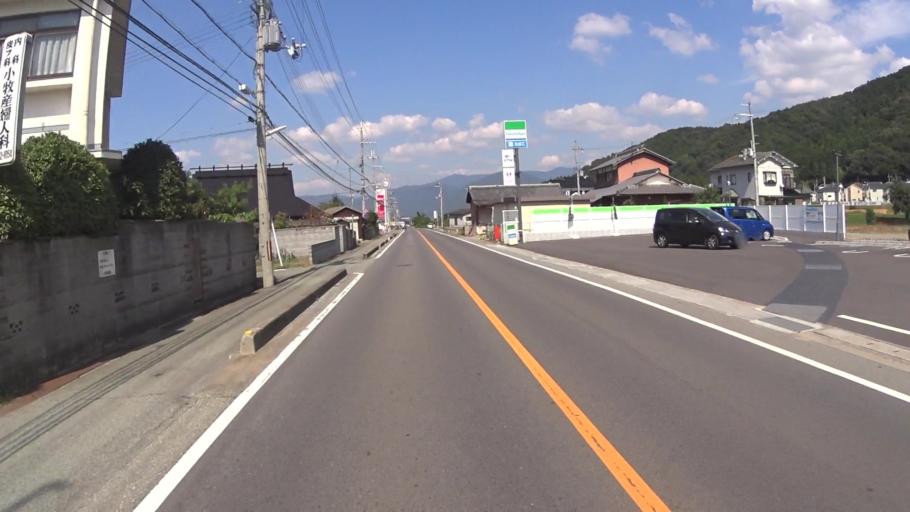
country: JP
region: Kyoto
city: Kameoka
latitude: 34.9995
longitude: 135.5525
